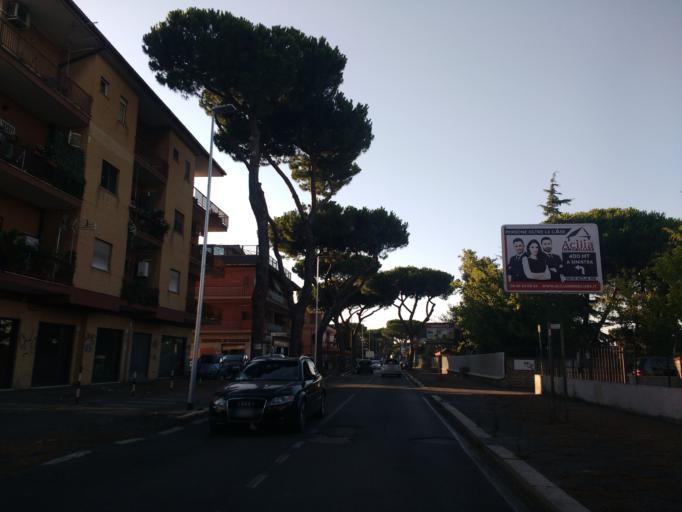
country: IT
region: Latium
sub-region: Citta metropolitana di Roma Capitale
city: Acilia-Castel Fusano-Ostia Antica
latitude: 41.7775
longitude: 12.3687
